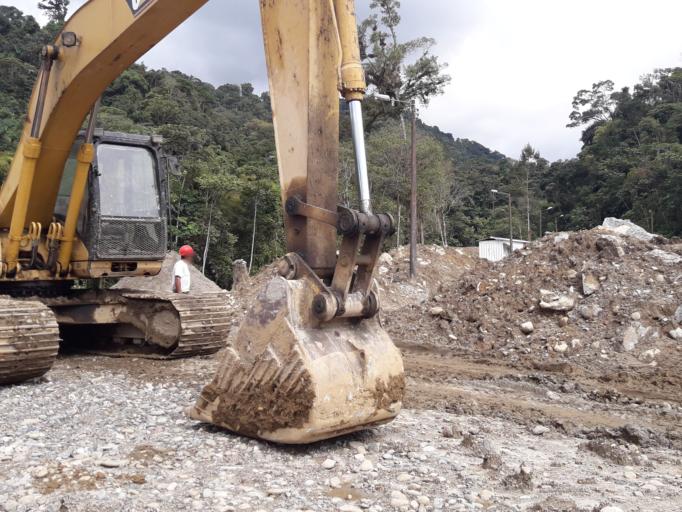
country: EC
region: Napo
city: Archidona
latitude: -0.9460
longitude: -77.8916
